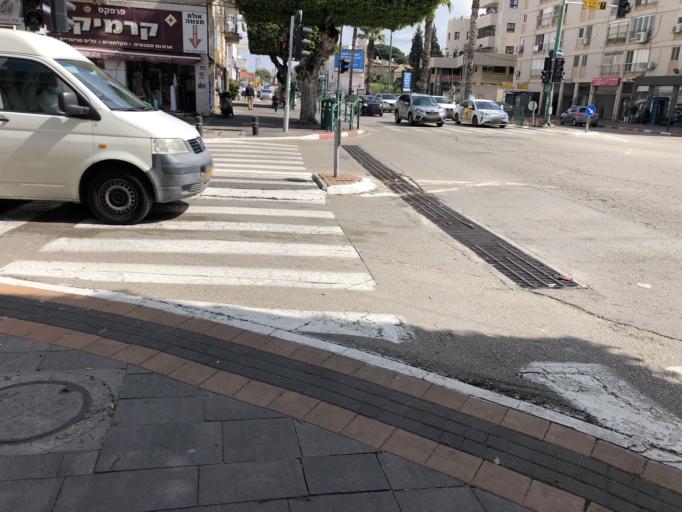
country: IL
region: Haifa
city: Hadera
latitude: 32.4382
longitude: 34.9258
